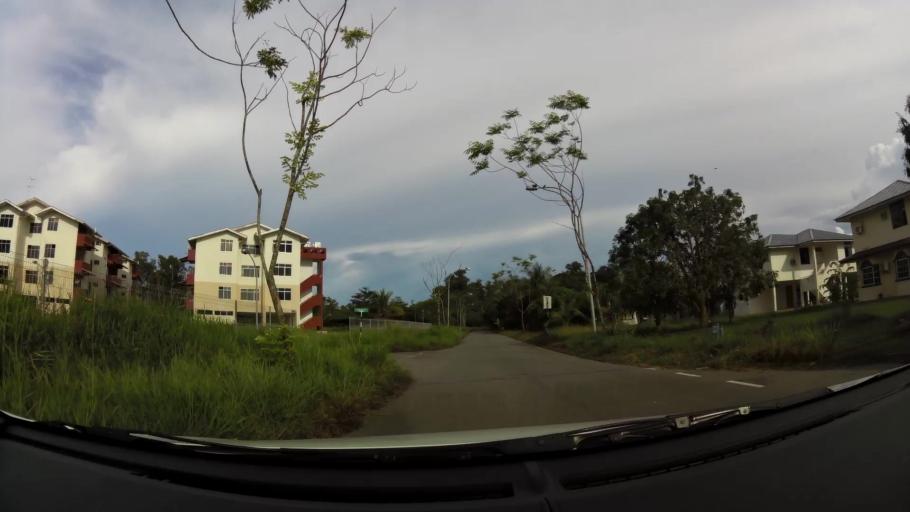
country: BN
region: Brunei and Muara
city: Bandar Seri Begawan
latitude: 4.9729
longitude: 115.0297
